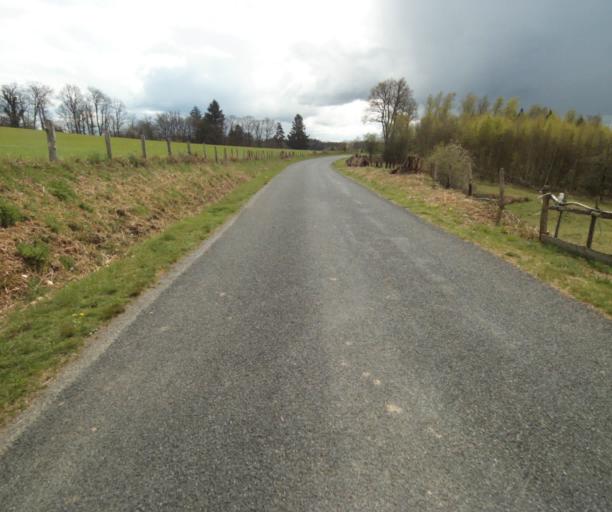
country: FR
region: Limousin
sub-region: Departement de la Correze
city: Laguenne
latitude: 45.2526
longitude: 1.8795
